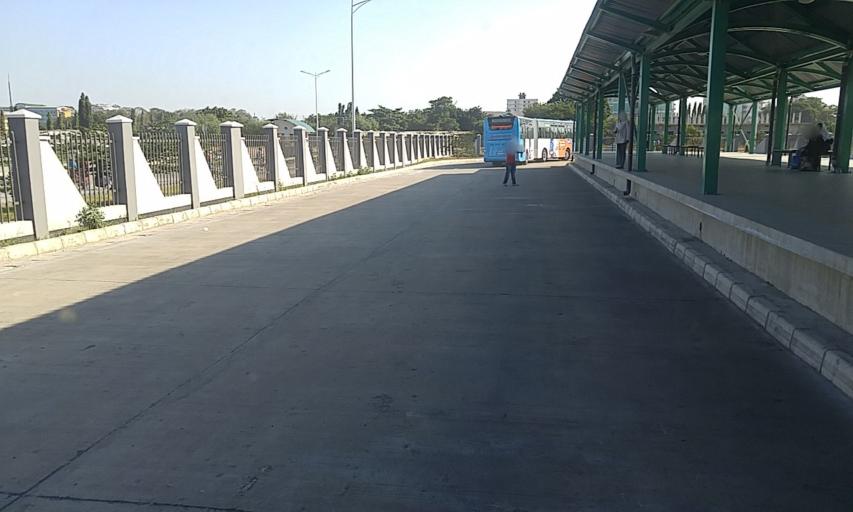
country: TZ
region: Dar es Salaam
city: Dar es Salaam
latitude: -6.8258
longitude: 39.2734
